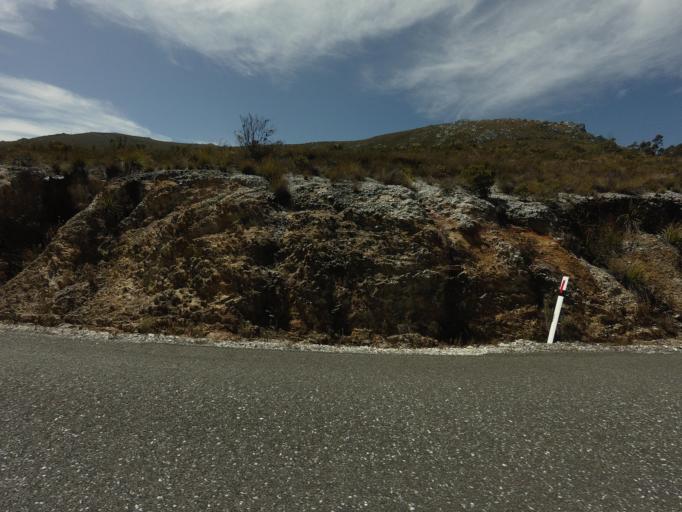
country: AU
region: Tasmania
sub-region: West Coast
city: Queenstown
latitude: -42.7915
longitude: 146.0633
